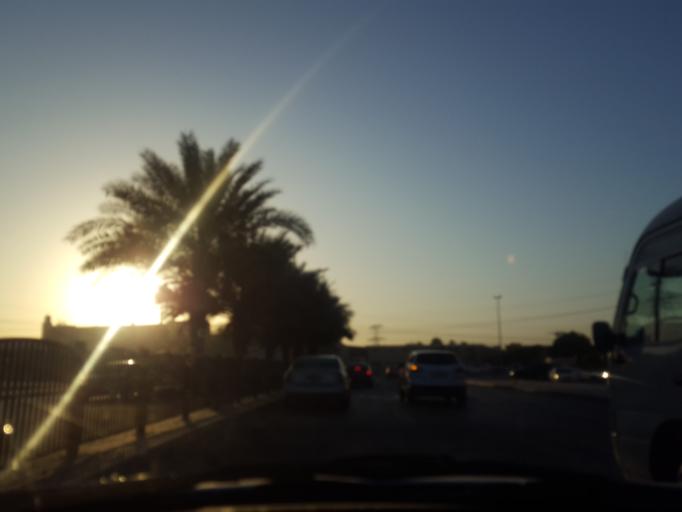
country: AE
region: Dubai
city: Dubai
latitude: 25.1385
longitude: 55.2557
